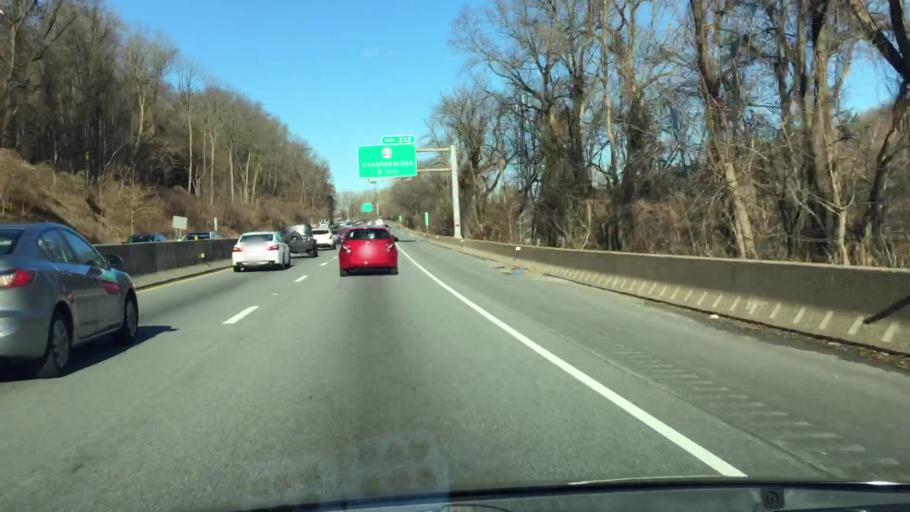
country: US
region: Pennsylvania
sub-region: Montgomery County
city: Conshohocken
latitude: 40.0652
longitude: -75.2772
